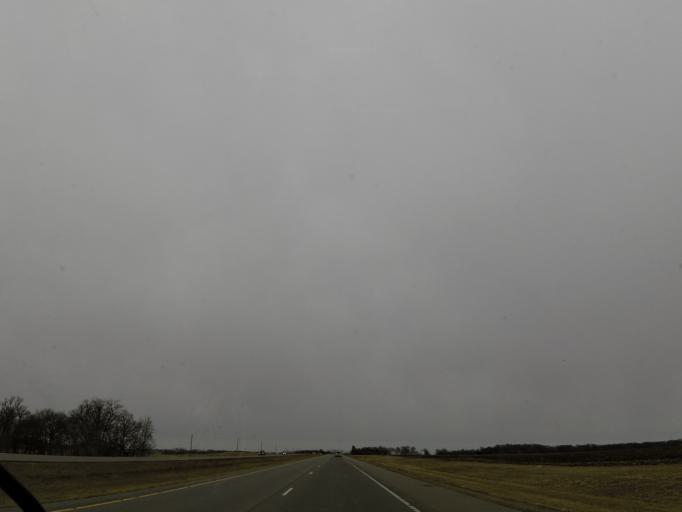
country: US
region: Minnesota
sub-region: Le Sueur County
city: Le Sueur
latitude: 44.5089
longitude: -93.8562
